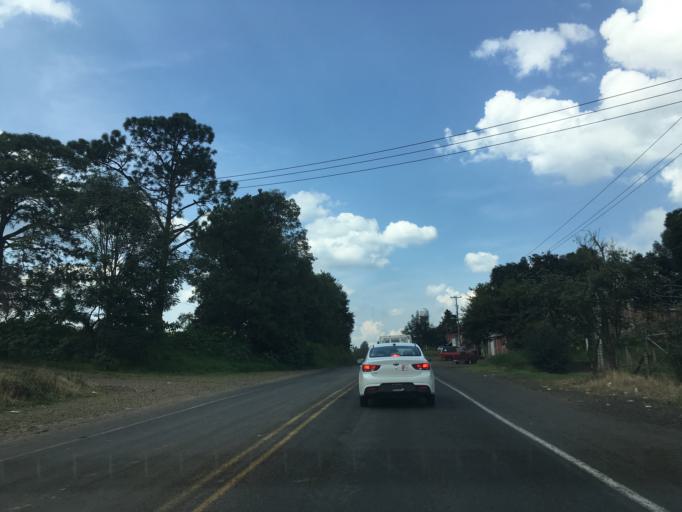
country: MX
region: Michoacan
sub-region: Tingueindin
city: Tingueindin
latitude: 19.7570
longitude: -102.4903
